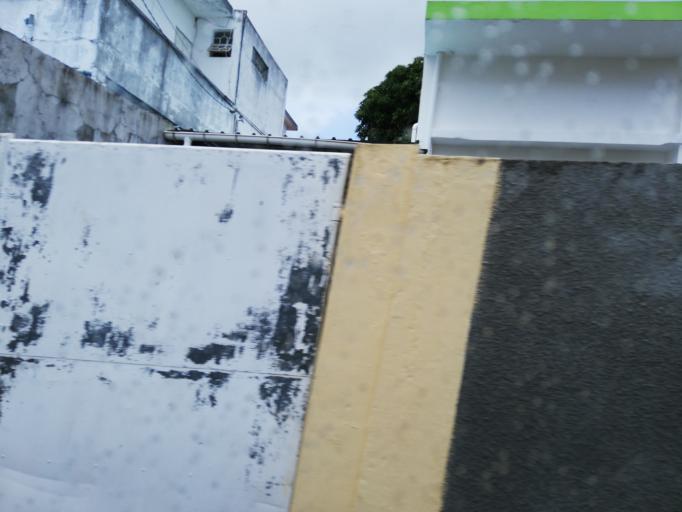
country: MU
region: Moka
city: Moka
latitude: -20.2166
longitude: 57.4714
